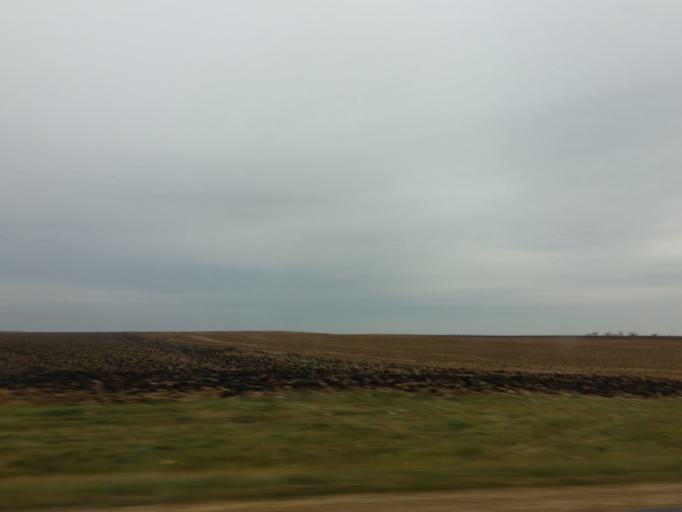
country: US
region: Iowa
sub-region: Black Hawk County
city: La Porte City
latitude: 42.2177
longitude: -92.2010
